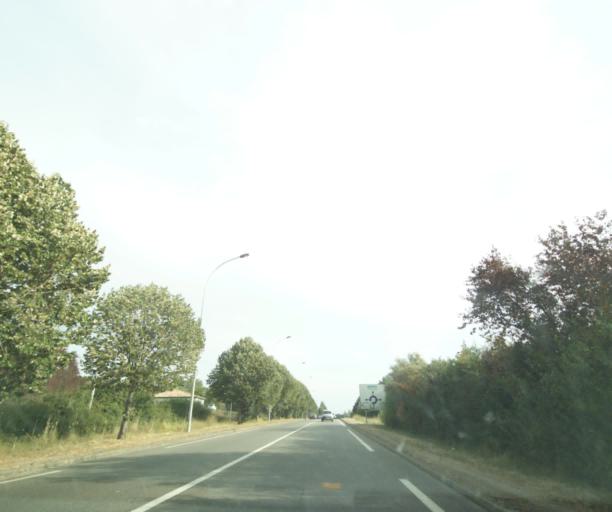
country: FR
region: Midi-Pyrenees
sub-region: Departement du Tarn-et-Garonne
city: Grisolles
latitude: 43.8316
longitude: 1.3020
